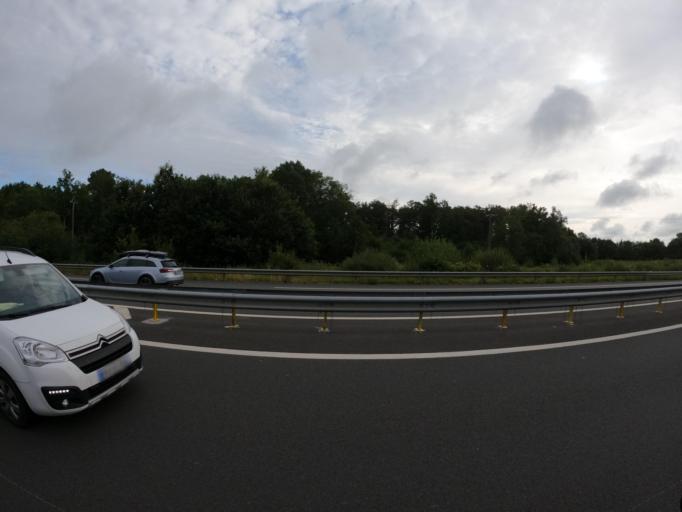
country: FR
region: Centre
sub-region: Departement d'Indre-et-Loire
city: Villandry
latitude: 47.3166
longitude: 0.5028
